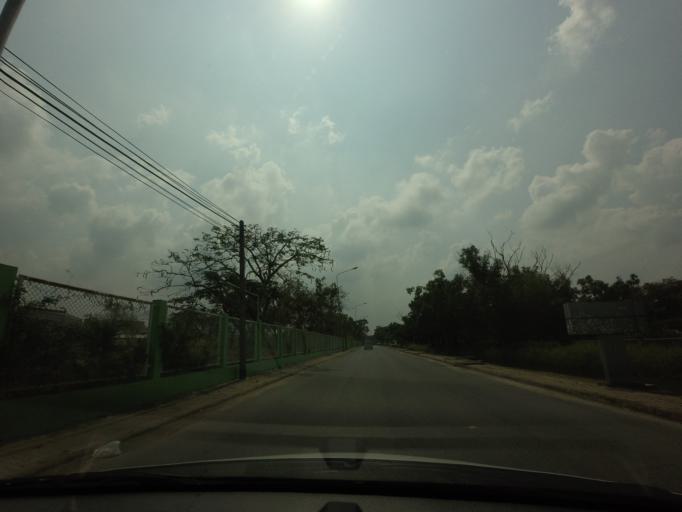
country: TH
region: Pathum Thani
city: Thanyaburi
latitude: 14.0469
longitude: 100.7163
